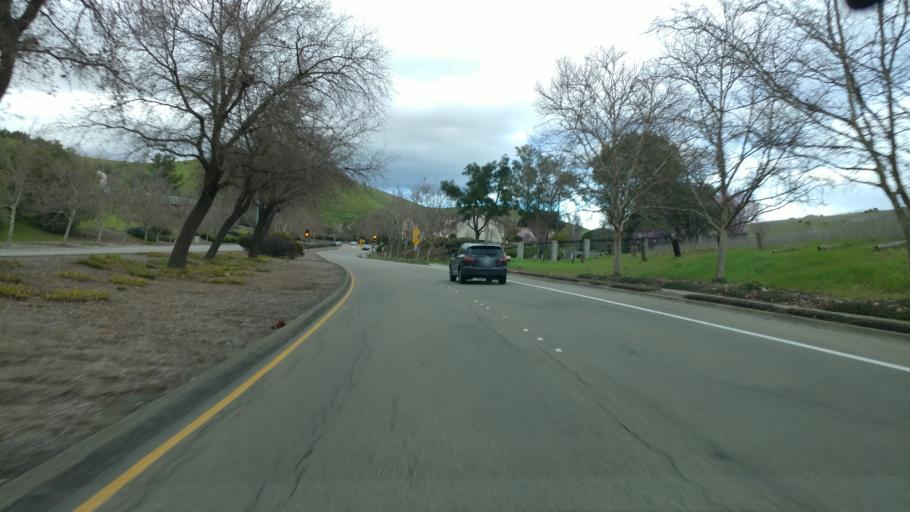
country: US
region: California
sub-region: Contra Costa County
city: San Ramon
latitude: 37.7847
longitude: -121.9356
